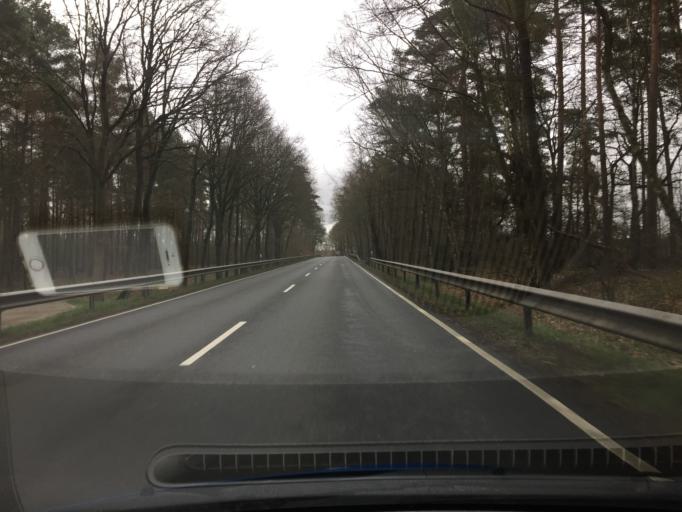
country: DE
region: Lower Saxony
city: Stoetze
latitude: 53.0436
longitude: 10.7985
